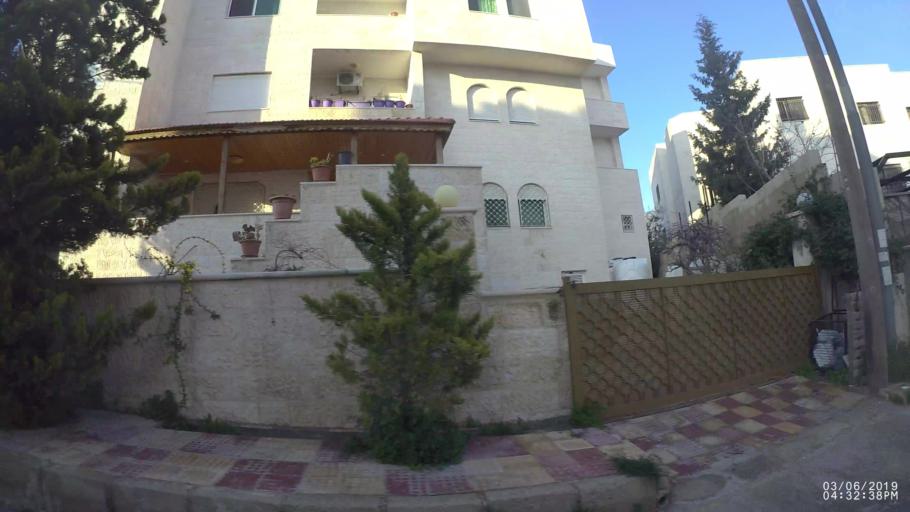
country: JO
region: Amman
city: Amman
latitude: 31.9849
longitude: 35.9604
